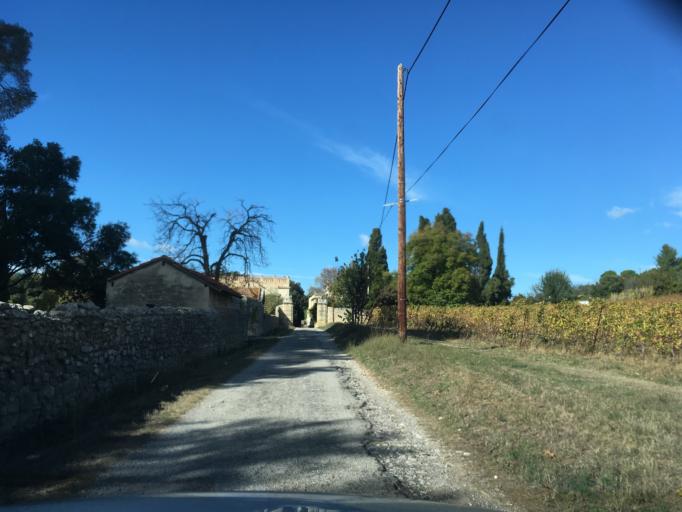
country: FR
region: Languedoc-Roussillon
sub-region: Departement de l'Herault
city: Saint-Jean-de-Vedas
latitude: 43.5871
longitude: 3.8471
